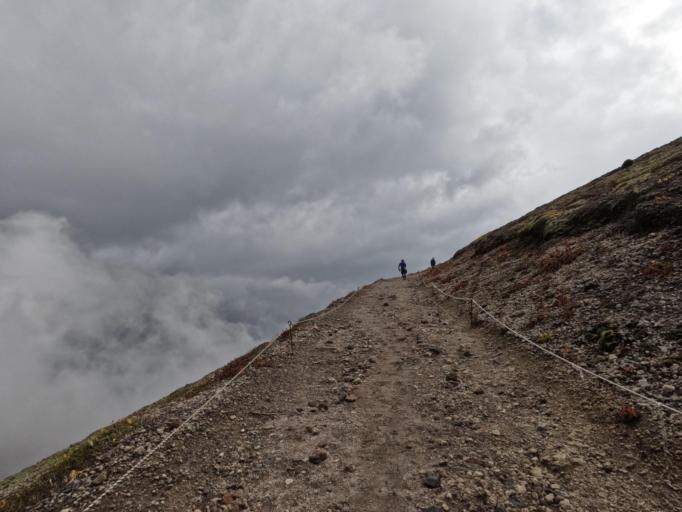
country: JP
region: Hokkaido
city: Shiraoi
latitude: 42.6931
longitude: 141.3905
